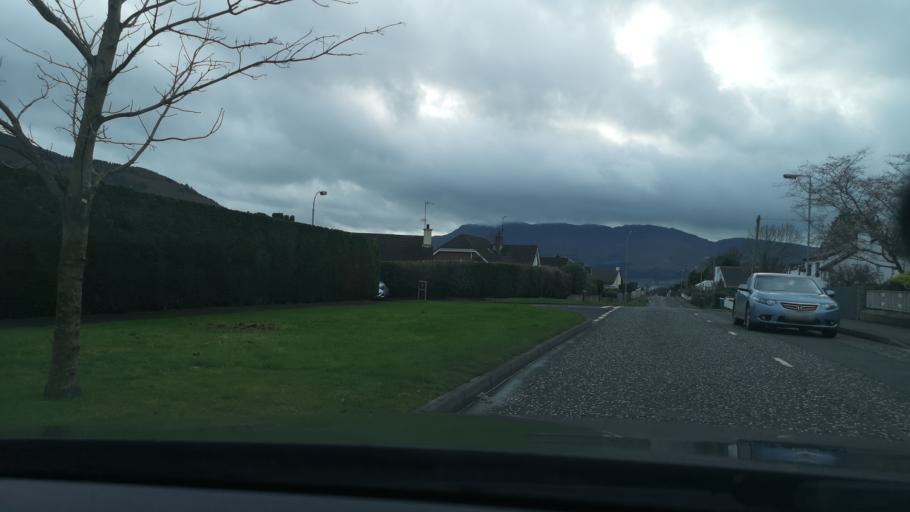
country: GB
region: Northern Ireland
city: Rostrevor
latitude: 54.1077
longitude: -6.1885
